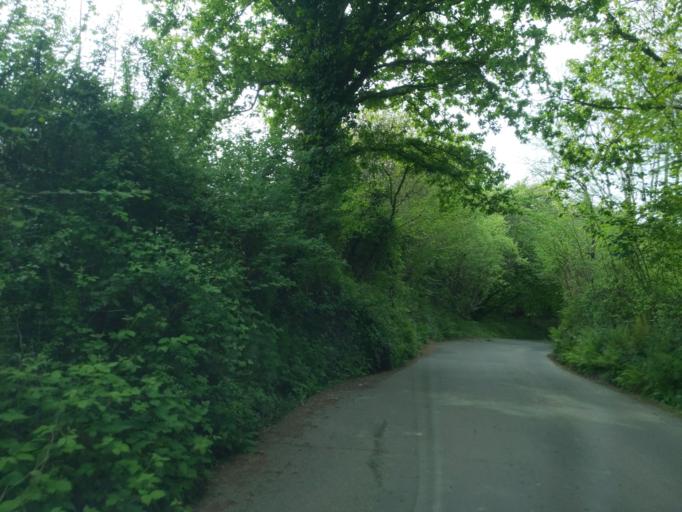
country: GB
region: England
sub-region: Devon
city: Plympton
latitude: 50.4320
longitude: -4.0579
